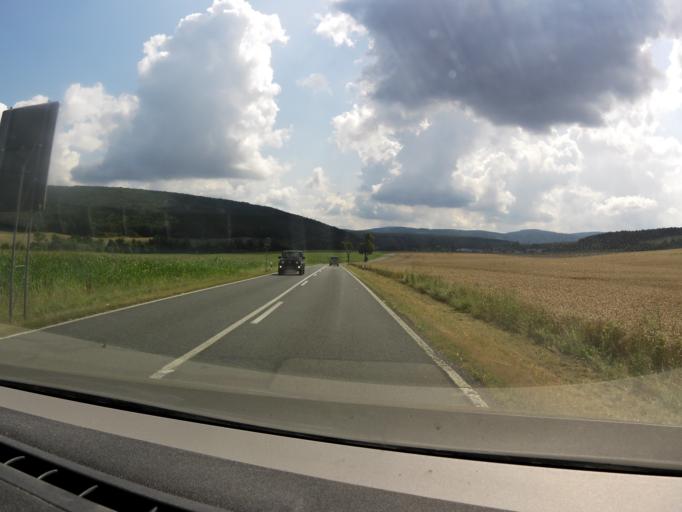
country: DE
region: Thuringia
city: Neusiss
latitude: 50.7407
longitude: 10.8888
